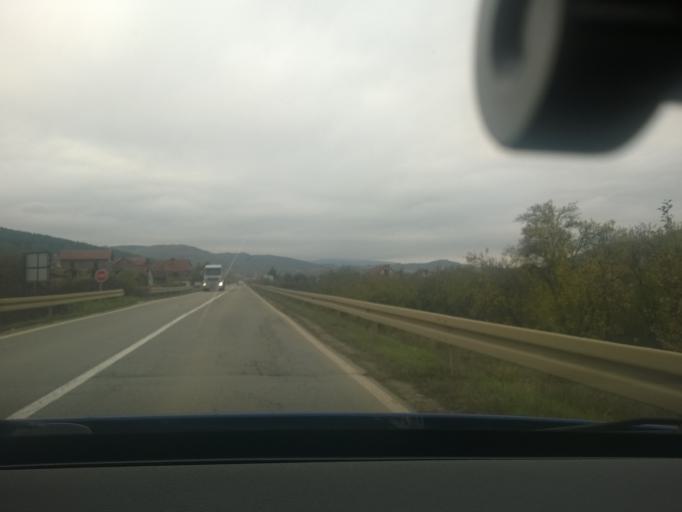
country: RS
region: Central Serbia
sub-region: Pirotski Okrug
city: Dimitrovgrad
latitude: 43.0100
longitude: 22.7551
